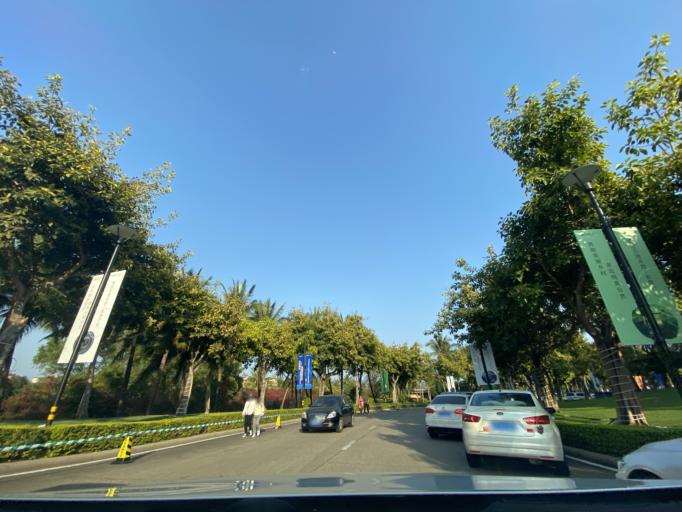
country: CN
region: Hainan
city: Yingzhou
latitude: 18.3949
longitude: 109.8572
